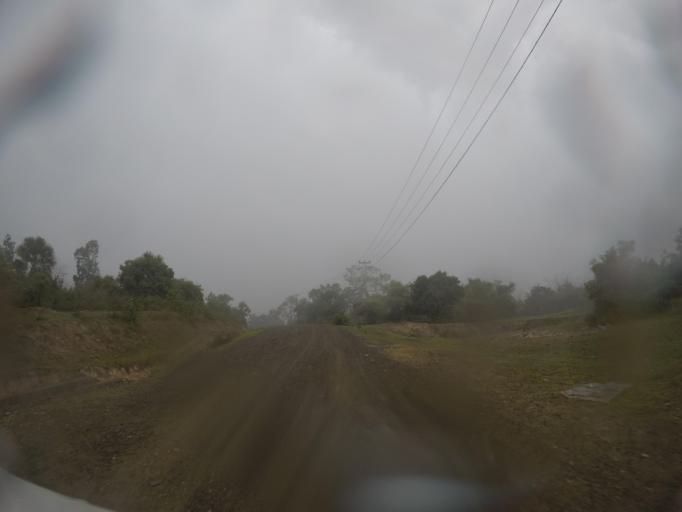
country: TL
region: Bobonaro
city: Maliana
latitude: -8.8577
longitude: 125.0865
